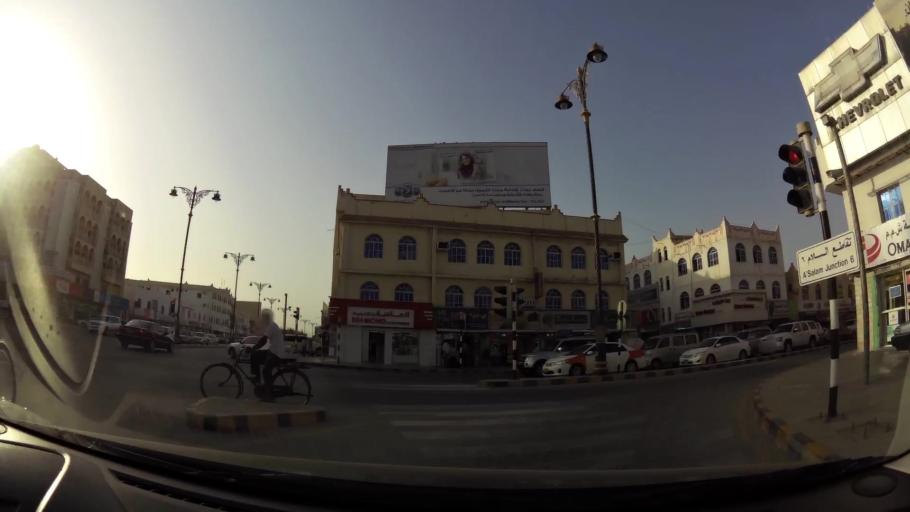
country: OM
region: Zufar
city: Salalah
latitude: 17.0126
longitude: 54.0939
